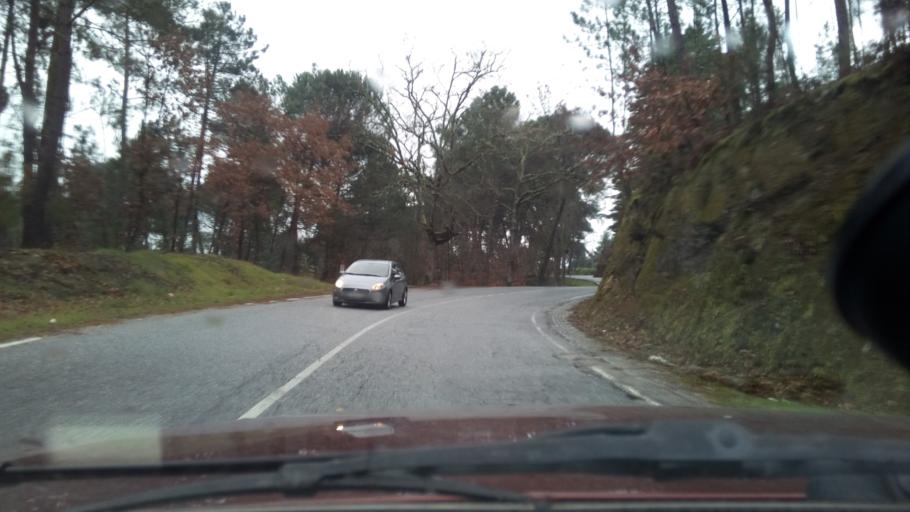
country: PT
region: Viseu
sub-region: Mangualde
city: Mangualde
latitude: 40.6325
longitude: -7.8053
